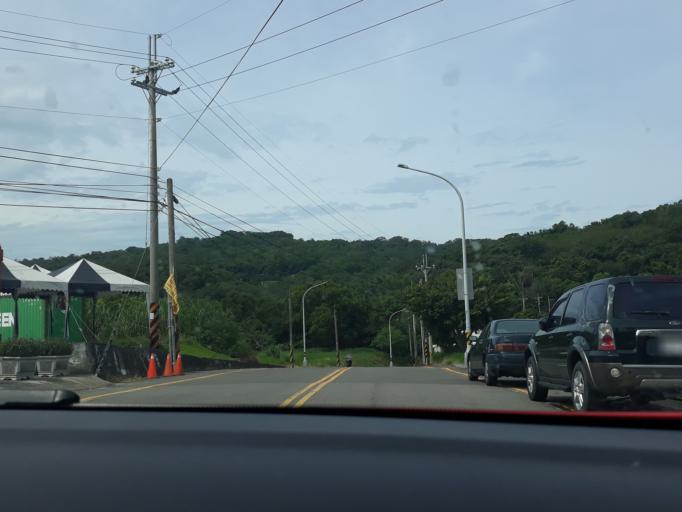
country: TW
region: Taiwan
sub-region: Miaoli
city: Miaoli
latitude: 24.5505
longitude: 120.8028
